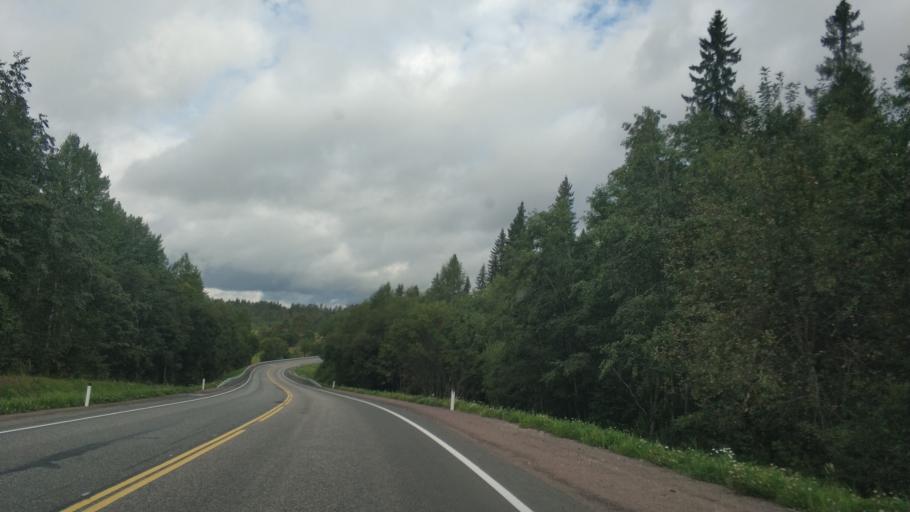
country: RU
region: Republic of Karelia
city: Khelyulya
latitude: 61.7954
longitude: 30.6218
